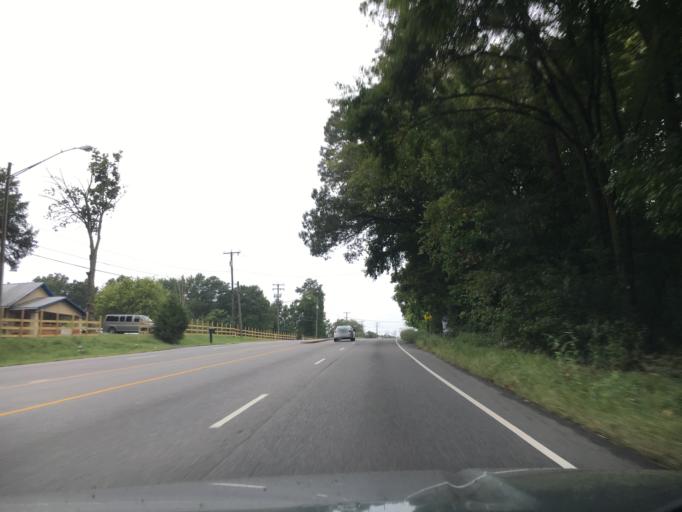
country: US
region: Virginia
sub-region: Chesterfield County
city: Bon Air
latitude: 37.4817
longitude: -77.5056
